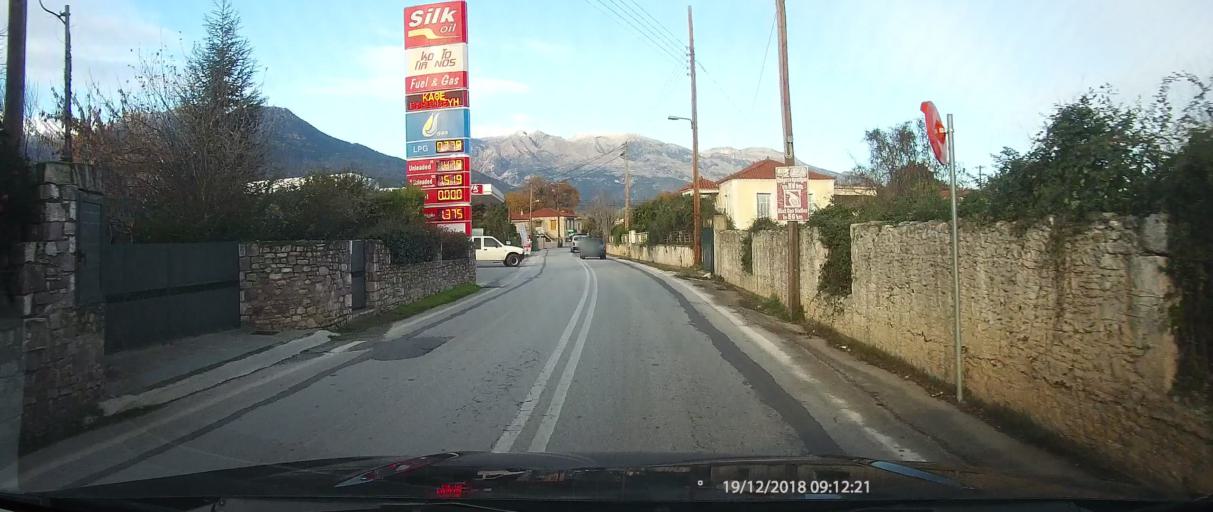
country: GR
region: Peloponnese
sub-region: Nomos Lakonias
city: Magoula
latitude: 37.0792
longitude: 22.4062
